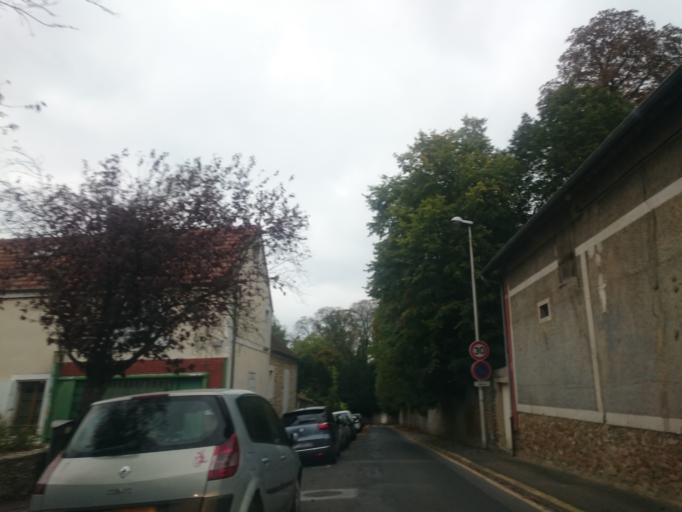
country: FR
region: Ile-de-France
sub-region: Departement de l'Essonne
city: Evry
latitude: 48.6318
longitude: 2.4482
